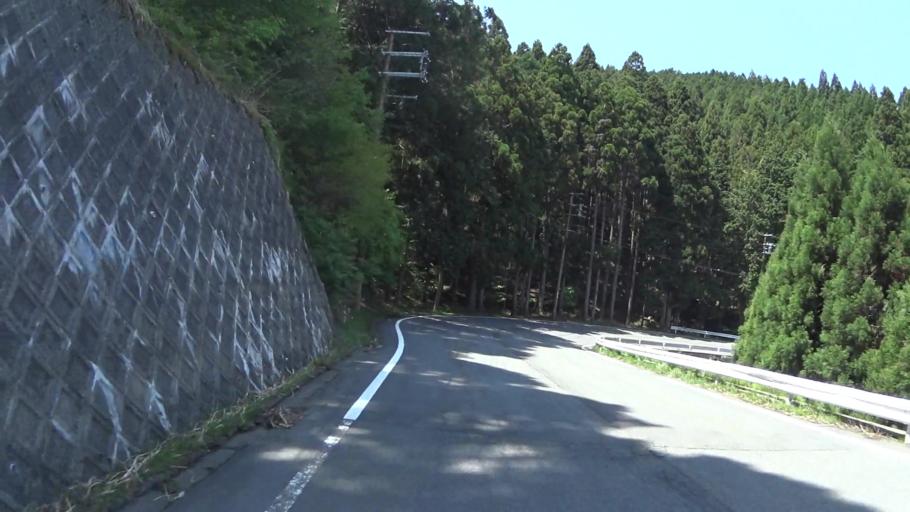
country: JP
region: Kyoto
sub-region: Kyoto-shi
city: Kamigyo-ku
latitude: 35.1568
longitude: 135.7828
